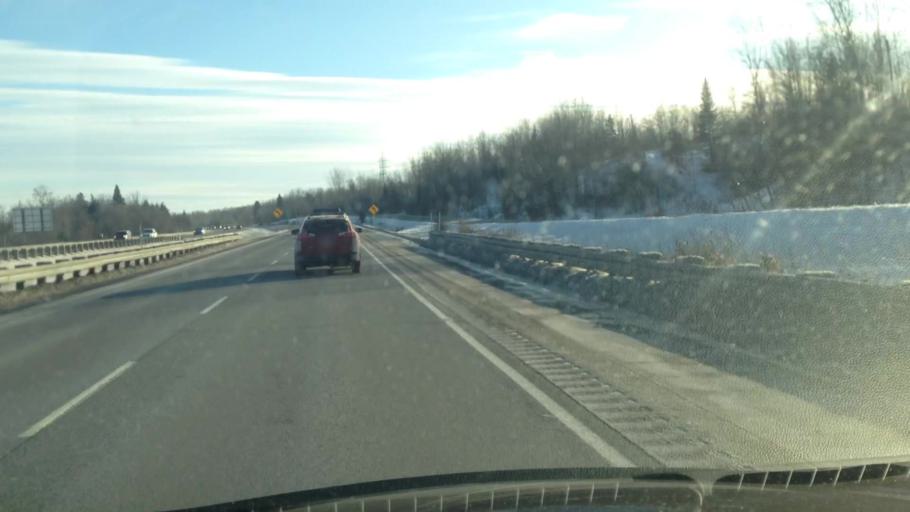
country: CA
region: Quebec
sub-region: Laurentides
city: Prevost
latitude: 45.8268
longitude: -74.0581
